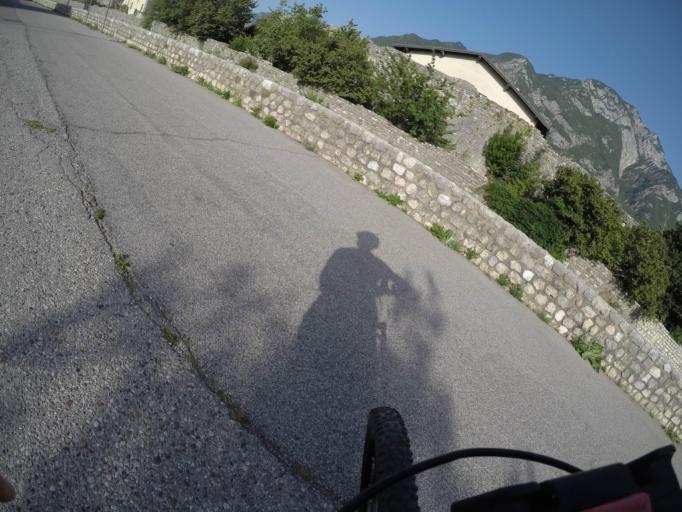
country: IT
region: Friuli Venezia Giulia
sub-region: Provincia di Udine
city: Venzone
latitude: 46.3347
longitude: 13.1411
